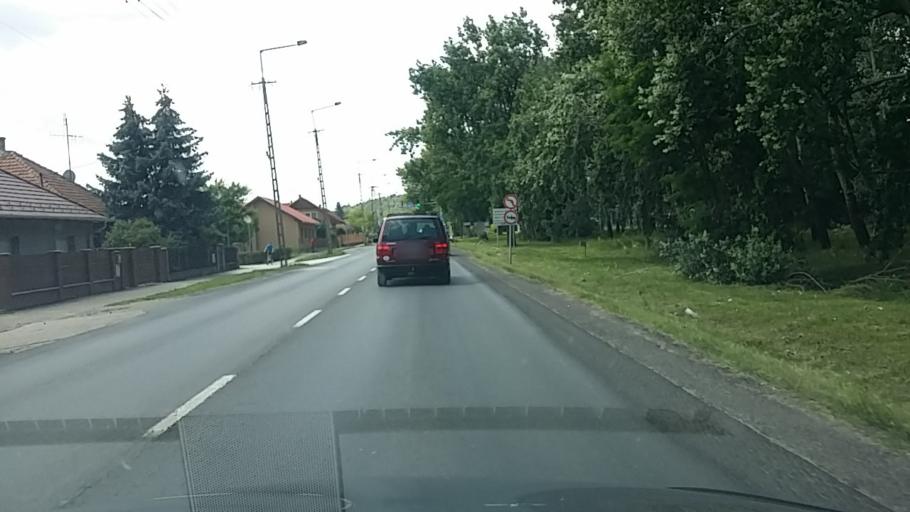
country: HU
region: Bacs-Kiskun
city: Kecskemet
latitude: 46.8909
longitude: 19.6526
